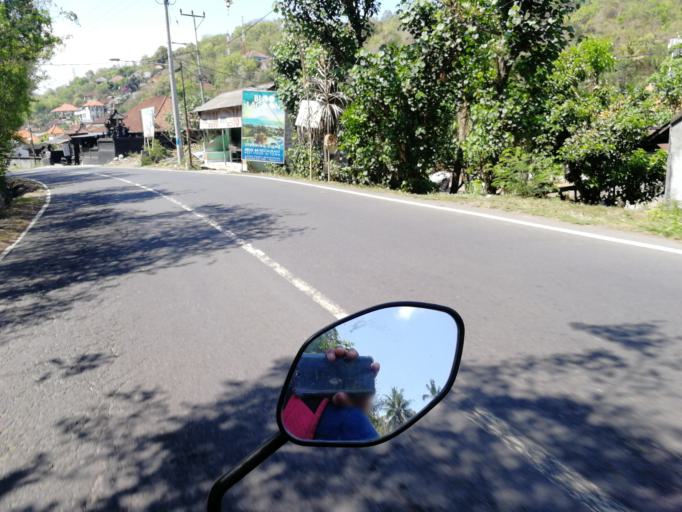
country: ID
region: Bali
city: Padangbai
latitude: -8.5289
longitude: 115.5048
